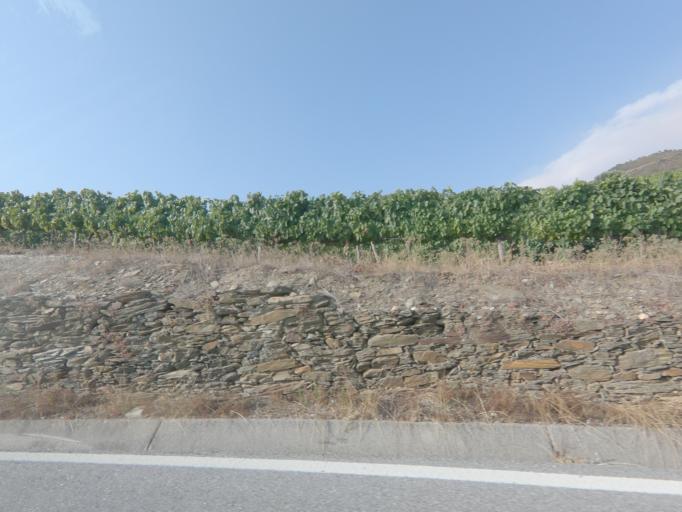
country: PT
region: Viseu
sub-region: Tabuaco
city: Tabuaco
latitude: 41.1373
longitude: -7.5365
